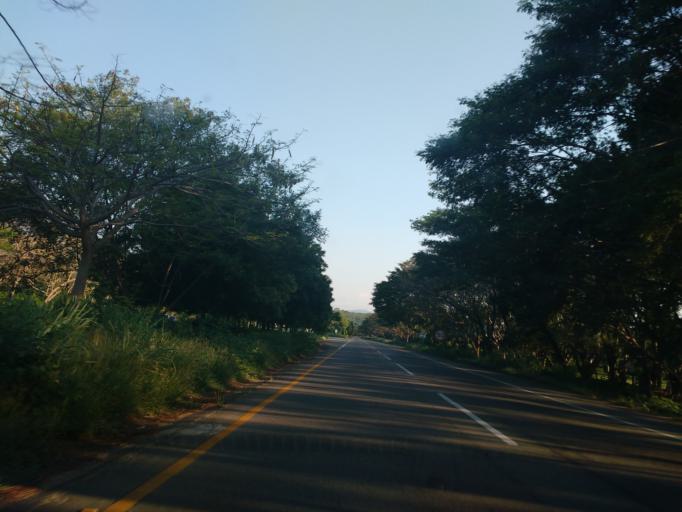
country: CO
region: Cundinamarca
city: Ricaurte
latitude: 4.2424
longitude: -74.7221
